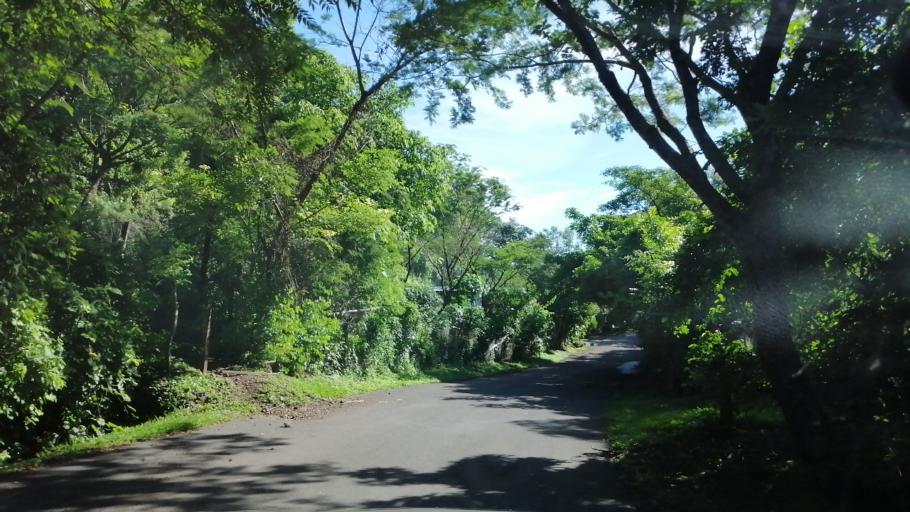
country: SV
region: Morazan
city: Cacaopera
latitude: 13.7850
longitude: -88.0336
